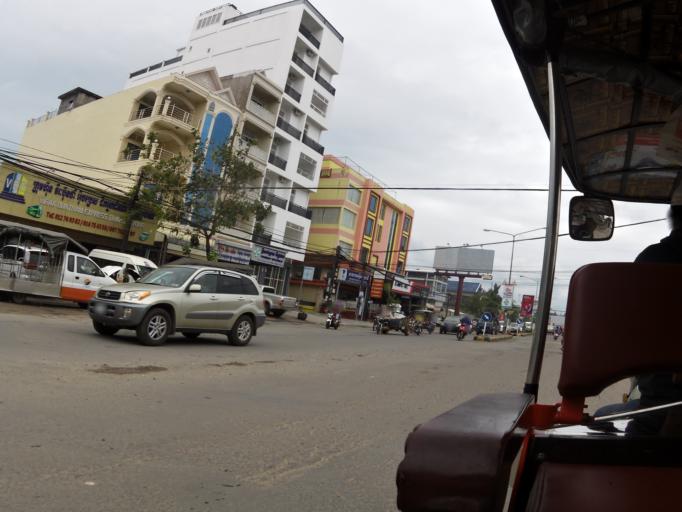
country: KH
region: Preah Sihanouk
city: Sihanoukville
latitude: 10.6243
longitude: 103.5215
